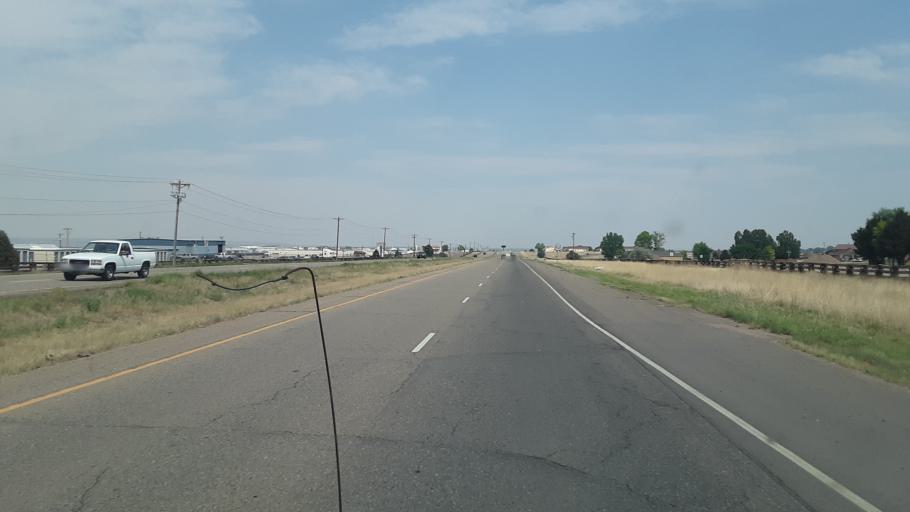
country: US
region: Colorado
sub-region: Pueblo County
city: Pueblo West
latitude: 38.3337
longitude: -104.7373
